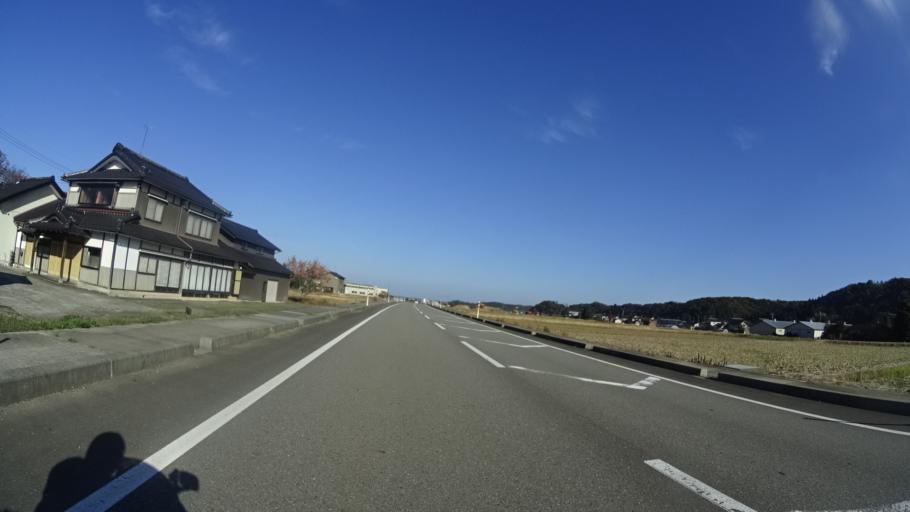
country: JP
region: Ishikawa
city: Komatsu
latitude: 36.2877
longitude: 136.3900
